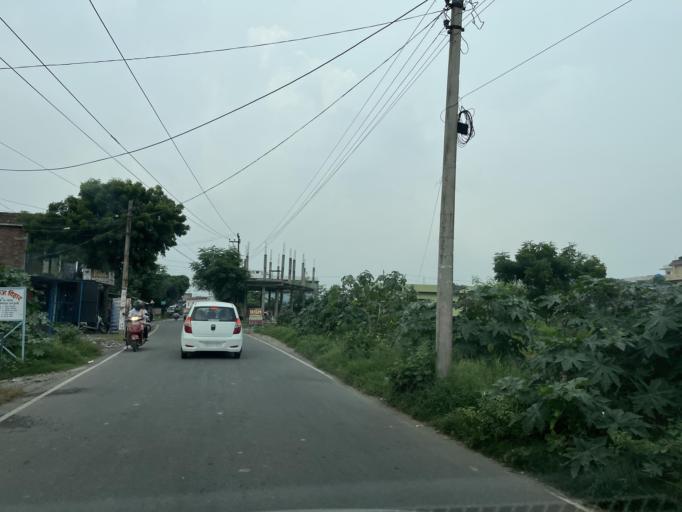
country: IN
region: Uttarakhand
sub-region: Naini Tal
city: Haldwani
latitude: 29.1964
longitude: 79.4853
